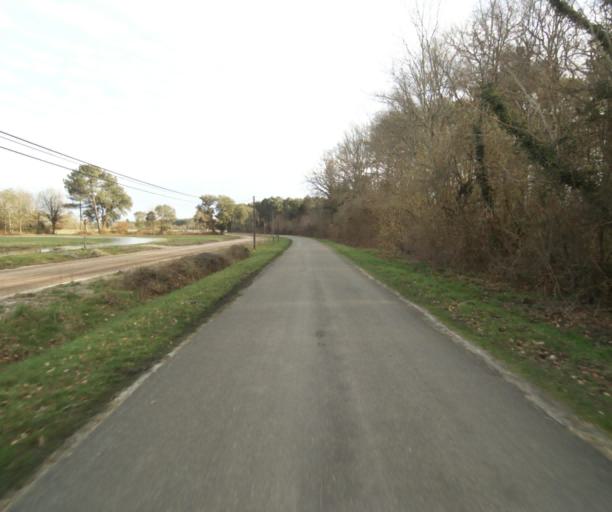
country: FR
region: Aquitaine
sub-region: Departement des Landes
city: Gabarret
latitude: 44.0488
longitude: 0.0566
